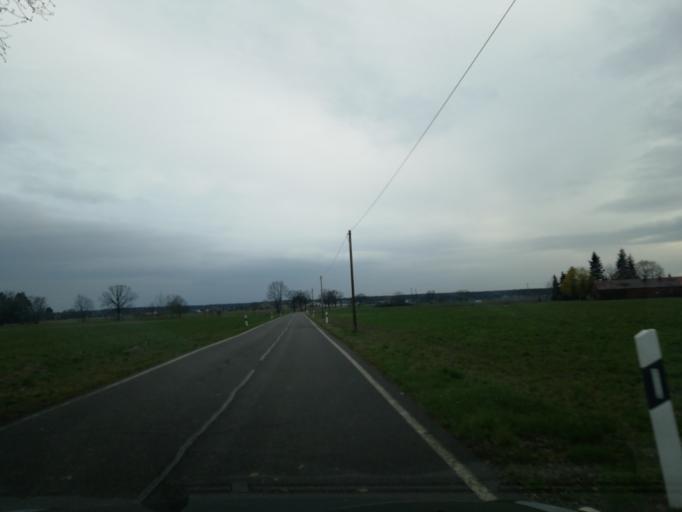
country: DE
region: Brandenburg
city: Vetschau
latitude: 51.7414
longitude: 14.0245
